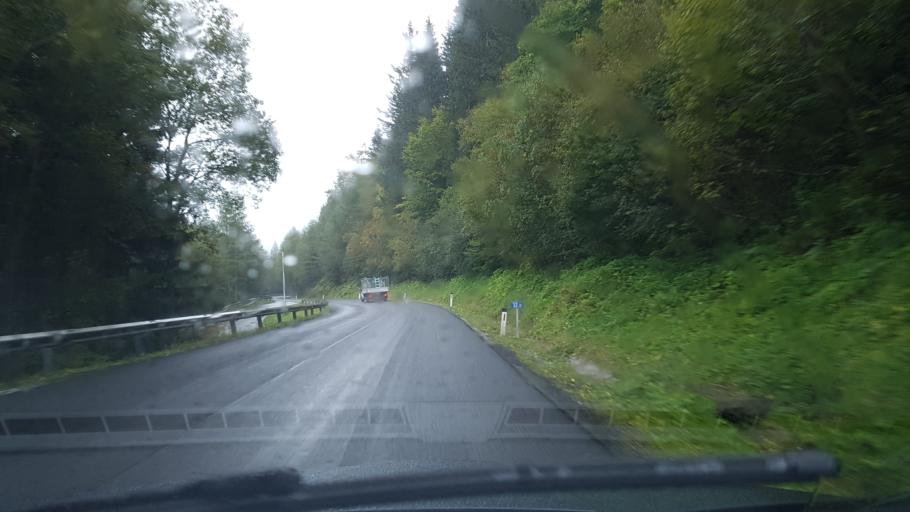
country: AT
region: Styria
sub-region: Politischer Bezirk Voitsberg
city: Salla
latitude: 47.1079
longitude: 14.9498
